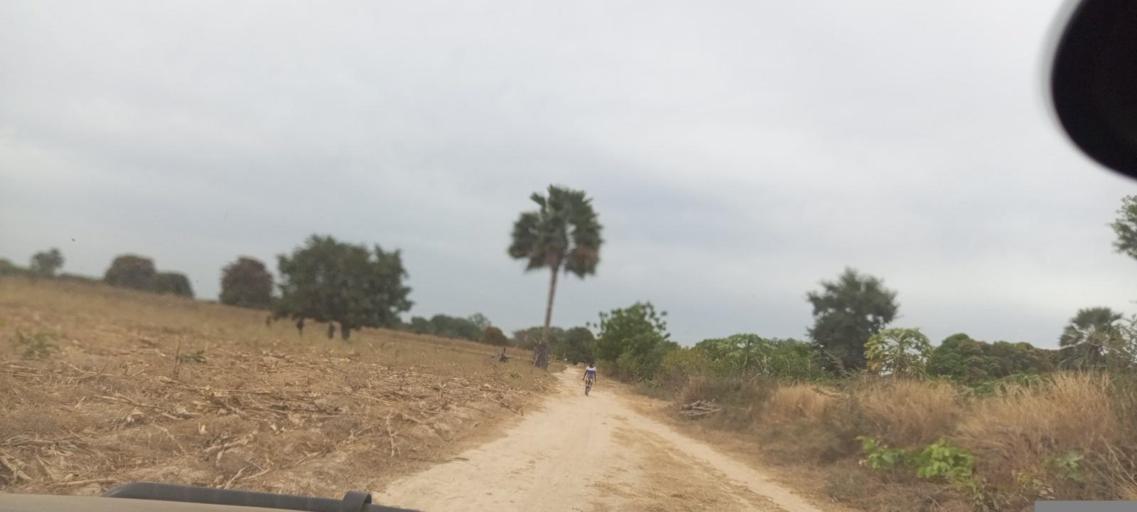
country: ML
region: Koulikoro
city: Kati
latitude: 12.7559
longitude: -8.3087
